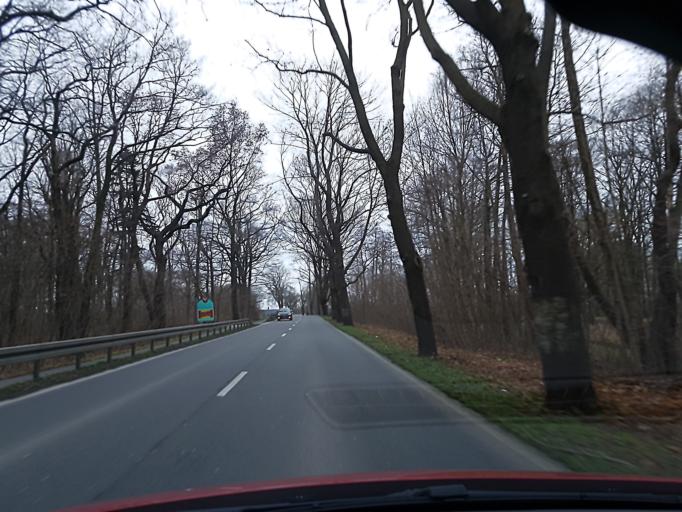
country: DE
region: Brandenburg
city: Elsterwerda
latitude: 51.4457
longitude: 13.5160
